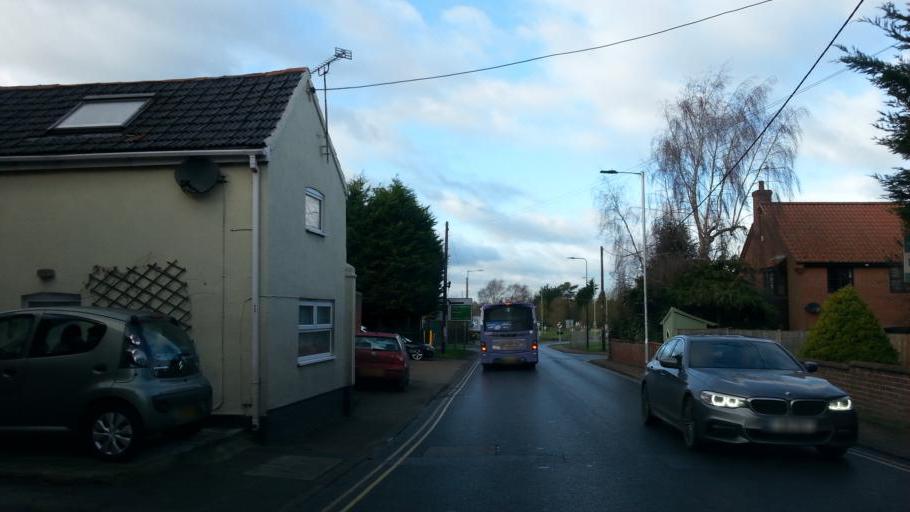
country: GB
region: England
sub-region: Suffolk
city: Bungay
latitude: 52.4585
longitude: 1.4343
